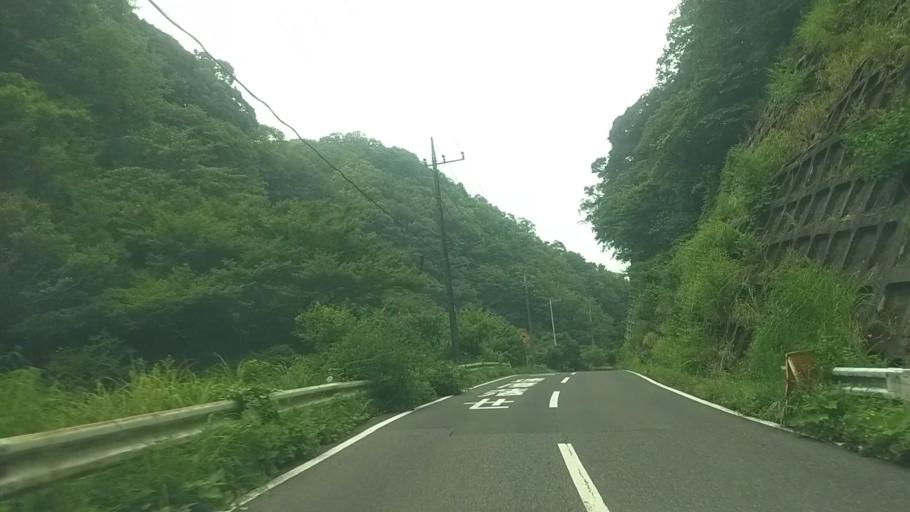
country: JP
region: Chiba
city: Kawaguchi
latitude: 35.2325
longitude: 140.0292
